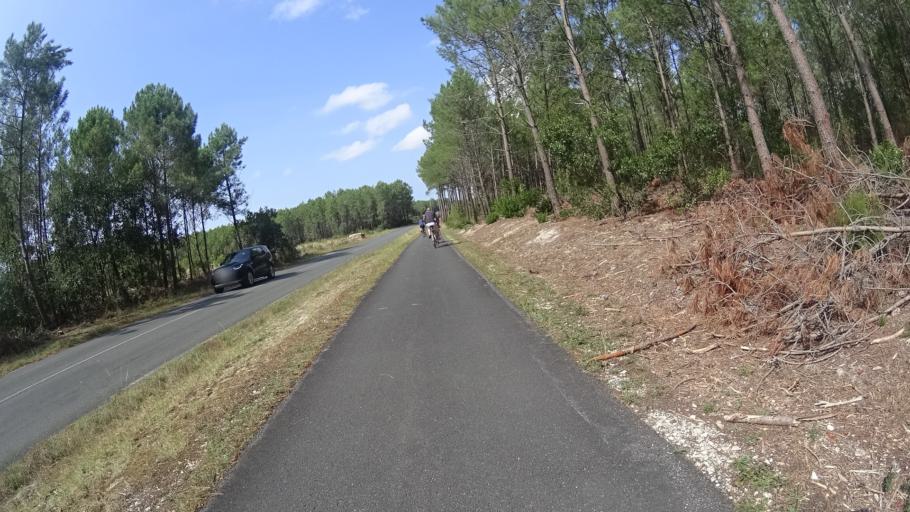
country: FR
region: Aquitaine
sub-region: Departement de la Gironde
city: Lacanau
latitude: 44.9839
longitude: -1.1437
